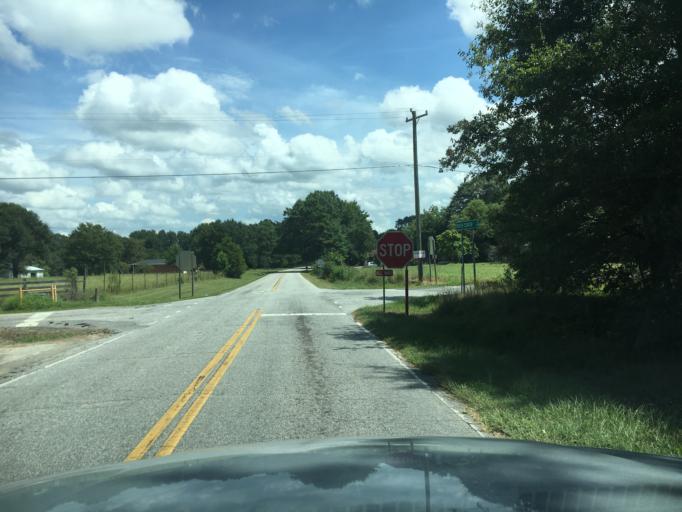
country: US
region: South Carolina
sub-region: Anderson County
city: Belton
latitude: 34.5691
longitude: -82.4870
